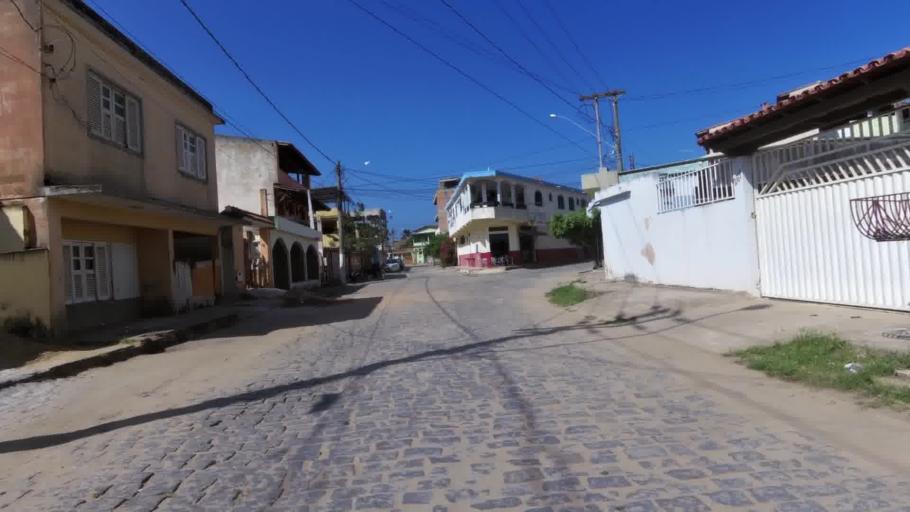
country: BR
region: Espirito Santo
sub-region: Marataizes
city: Marataizes
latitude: -21.0349
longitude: -40.8214
